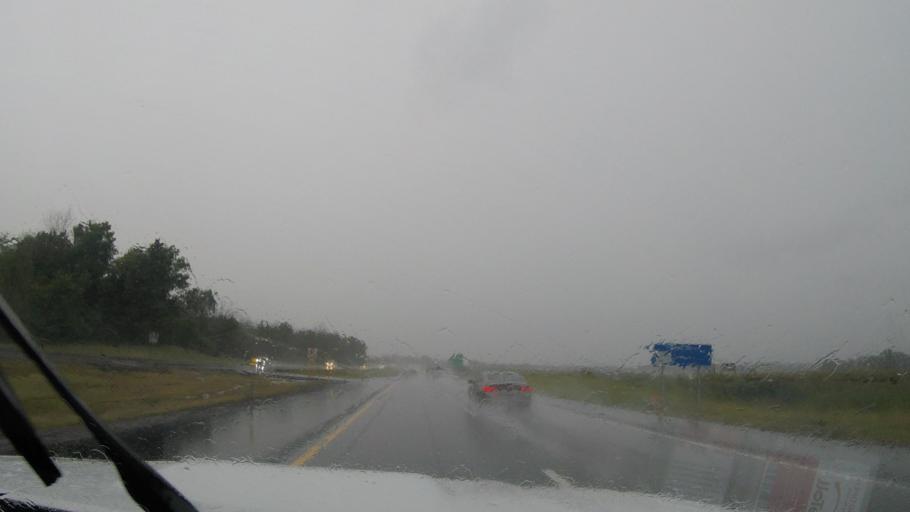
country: US
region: New York
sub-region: Seneca County
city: Waterloo
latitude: 42.9659
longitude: -76.8615
